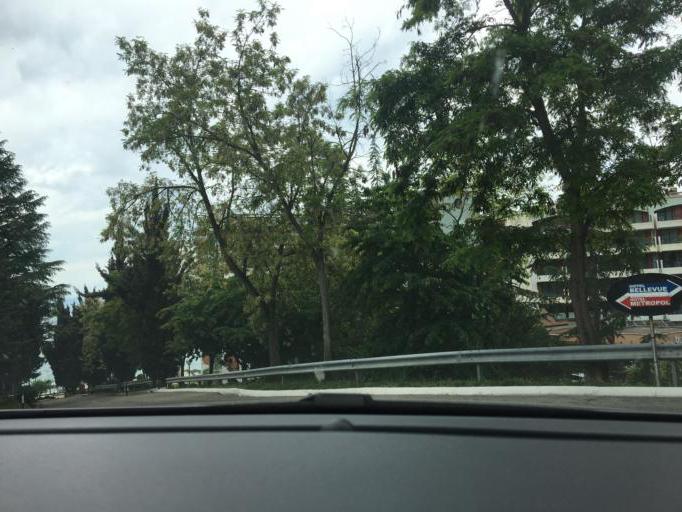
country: MK
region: Ohrid
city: Ohrid
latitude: 41.0580
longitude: 20.8027
